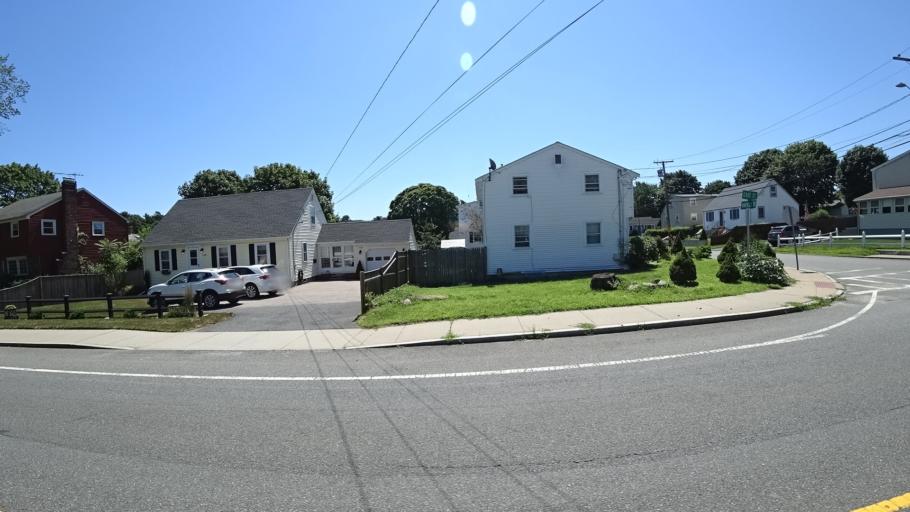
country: US
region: Massachusetts
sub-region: Norfolk County
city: Dedham
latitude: 42.2246
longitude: -71.1649
